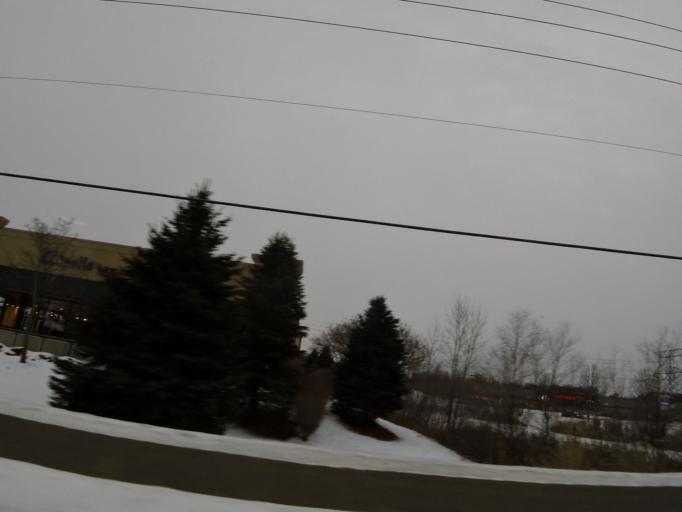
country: US
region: Minnesota
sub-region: Washington County
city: Stillwater
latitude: 45.0359
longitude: -92.8376
